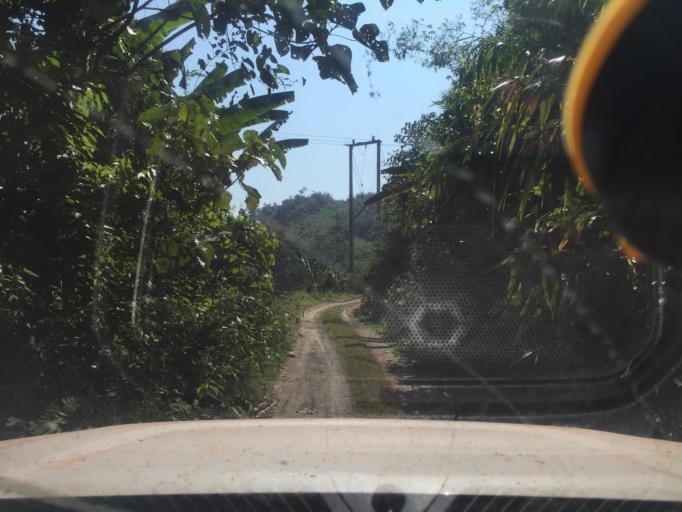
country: LA
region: Phongsali
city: Phongsali
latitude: 21.6881
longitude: 102.4094
